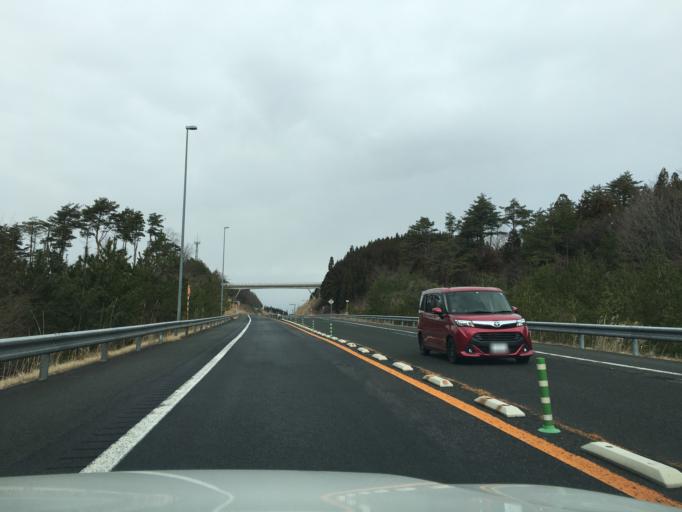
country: JP
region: Akita
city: Tenno
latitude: 40.0037
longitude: 140.0900
